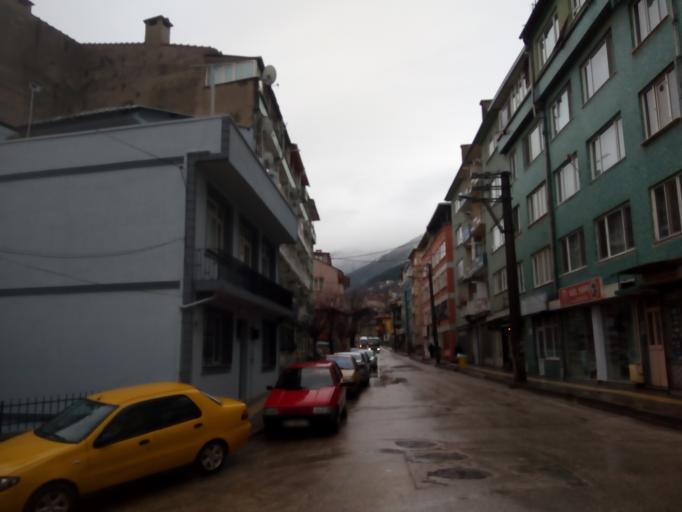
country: TR
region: Bursa
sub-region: Osmangazi
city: Bursa
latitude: 40.1783
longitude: 29.0599
